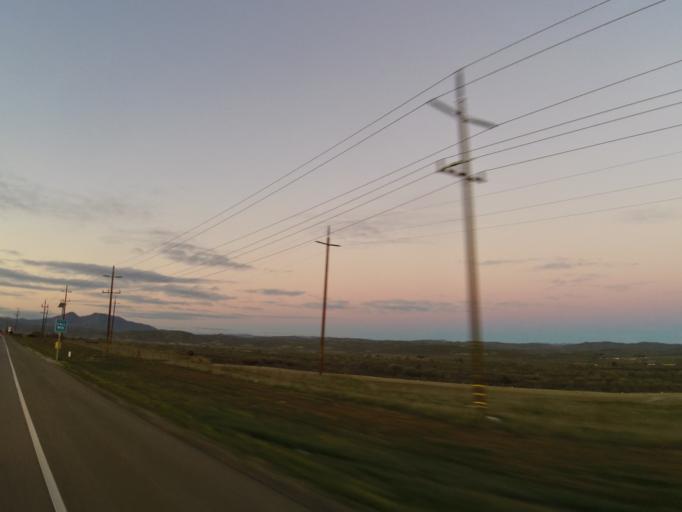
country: US
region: California
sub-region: Monterey County
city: King City
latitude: 36.2664
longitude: -121.1802
